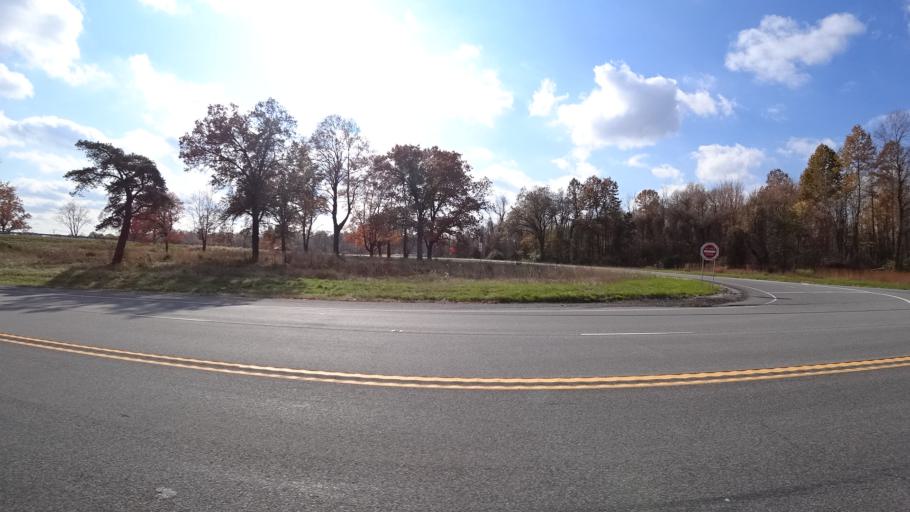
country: US
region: Indiana
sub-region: LaPorte County
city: Trail Creek
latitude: 41.6986
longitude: -86.8292
